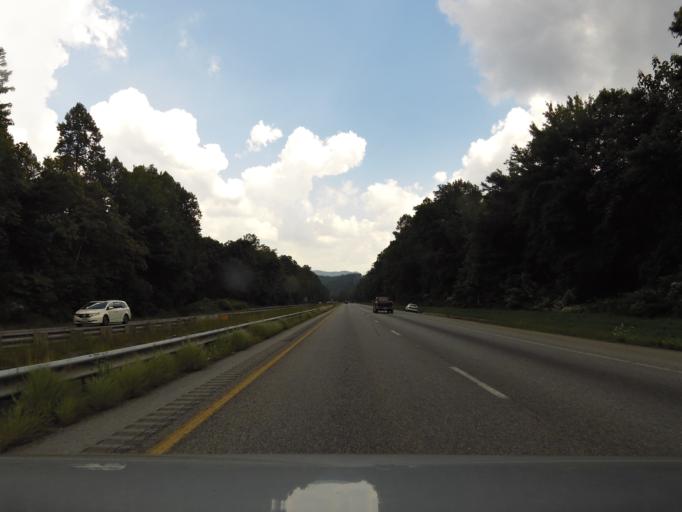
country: US
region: North Carolina
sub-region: Polk County
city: Tryon
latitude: 35.2466
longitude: -82.3135
